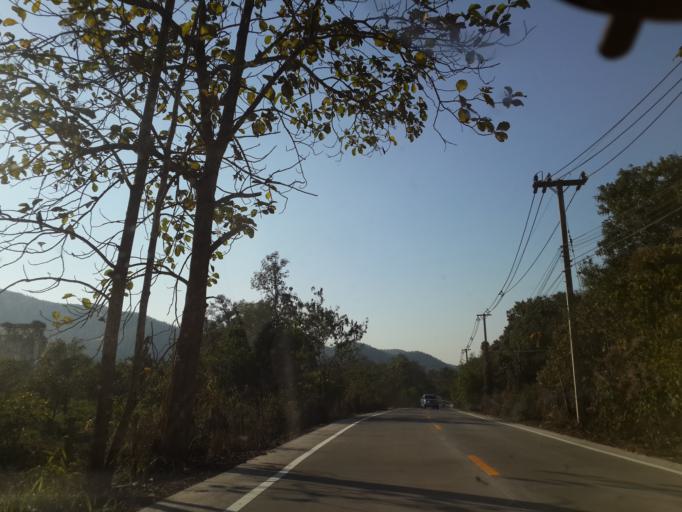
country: TH
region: Chiang Mai
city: Mae On
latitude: 18.8120
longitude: 99.2348
